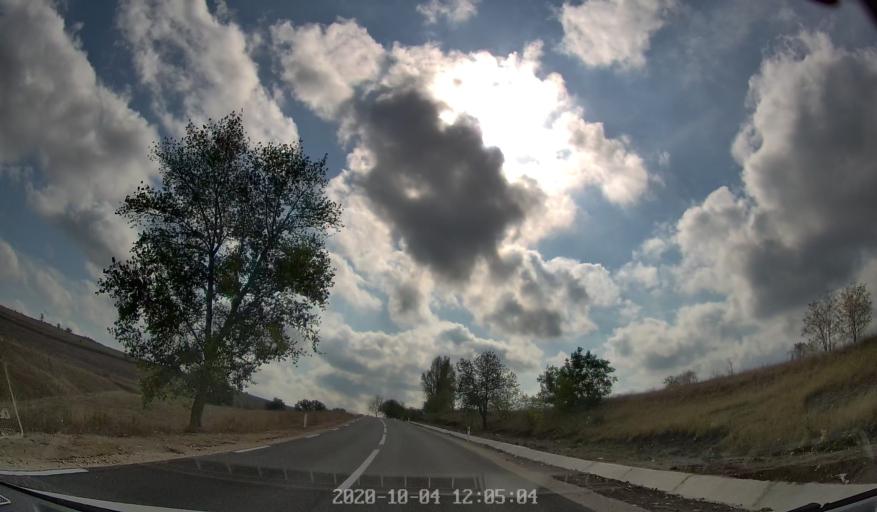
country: MD
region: Rezina
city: Saharna
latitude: 47.5974
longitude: 28.9486
